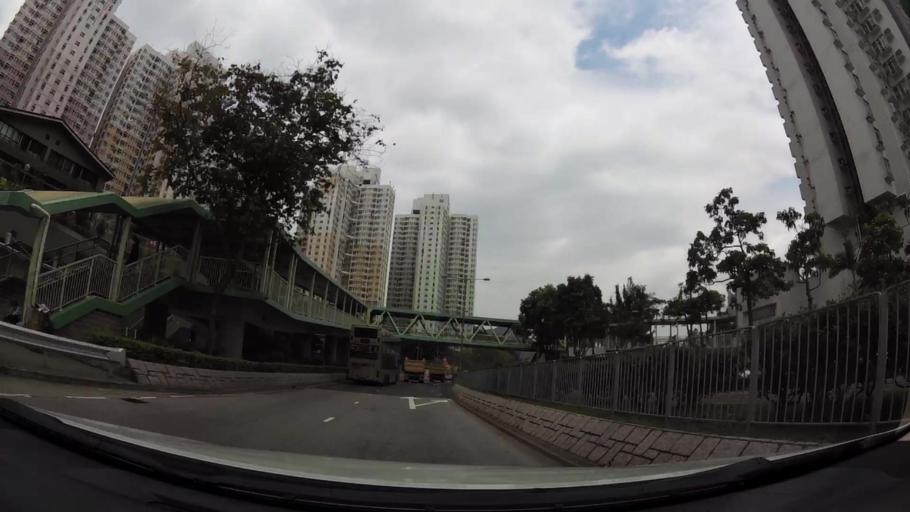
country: HK
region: Tuen Mun
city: Tuen Mun
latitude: 22.4090
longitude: 113.9672
